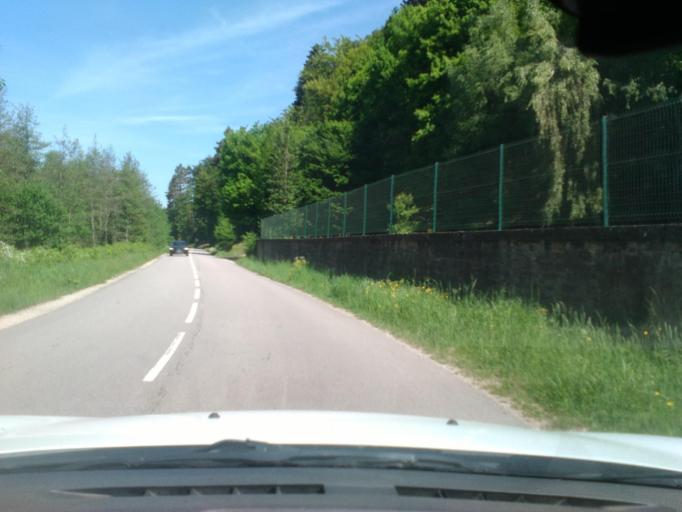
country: FR
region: Lorraine
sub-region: Departement des Vosges
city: Bruyeres
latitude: 48.2484
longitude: 6.7315
